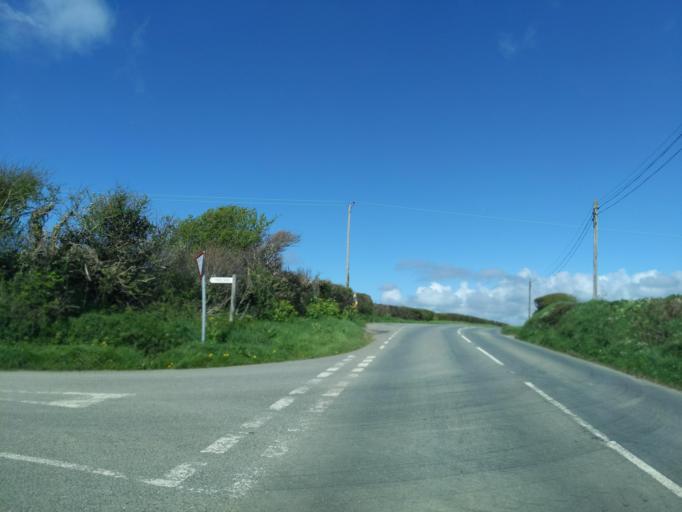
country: GB
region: England
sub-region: Cornwall
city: Wadebridge
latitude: 50.5850
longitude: -4.7852
